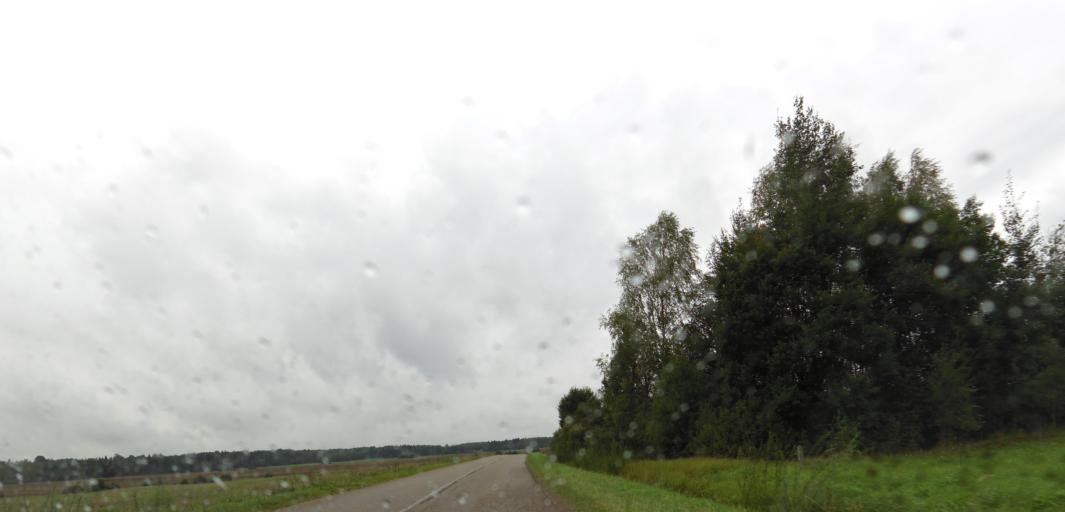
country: LT
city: Sirvintos
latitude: 55.0719
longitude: 25.0301
